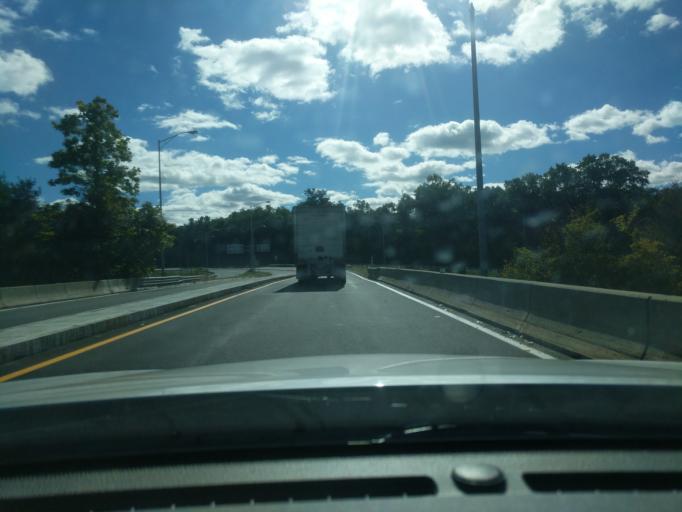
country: US
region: Massachusetts
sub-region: Hampden County
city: Westfield
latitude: 42.1452
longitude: -72.7353
